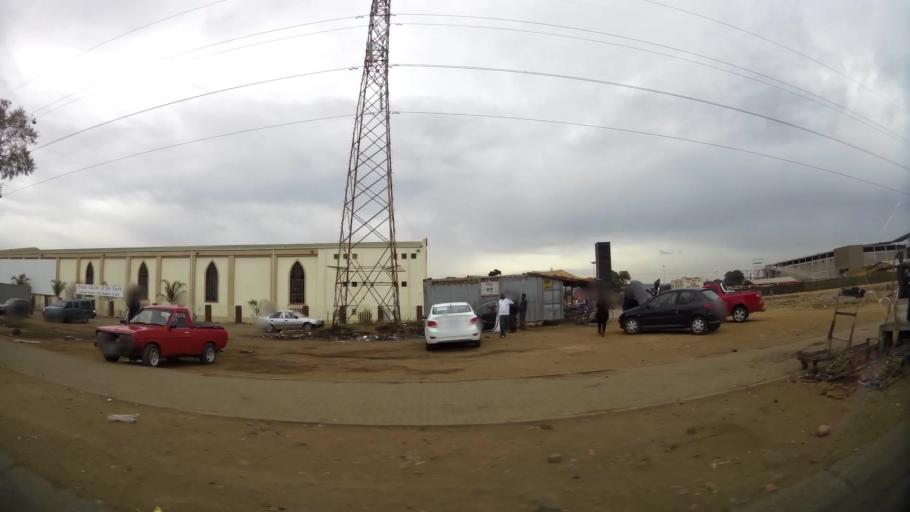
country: ZA
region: Gauteng
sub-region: City of Tshwane Metropolitan Municipality
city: Pretoria
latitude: -25.7184
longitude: 28.3439
